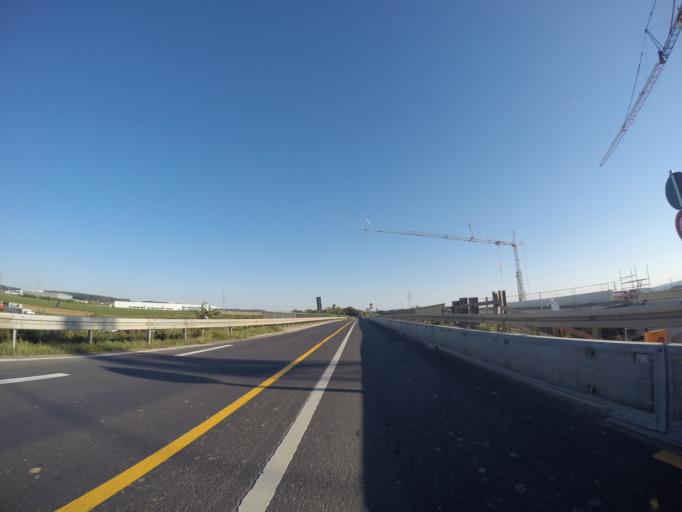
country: DE
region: Bavaria
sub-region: Regierungsbezirk Unterfranken
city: Esselbach
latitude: 49.8173
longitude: 9.5581
